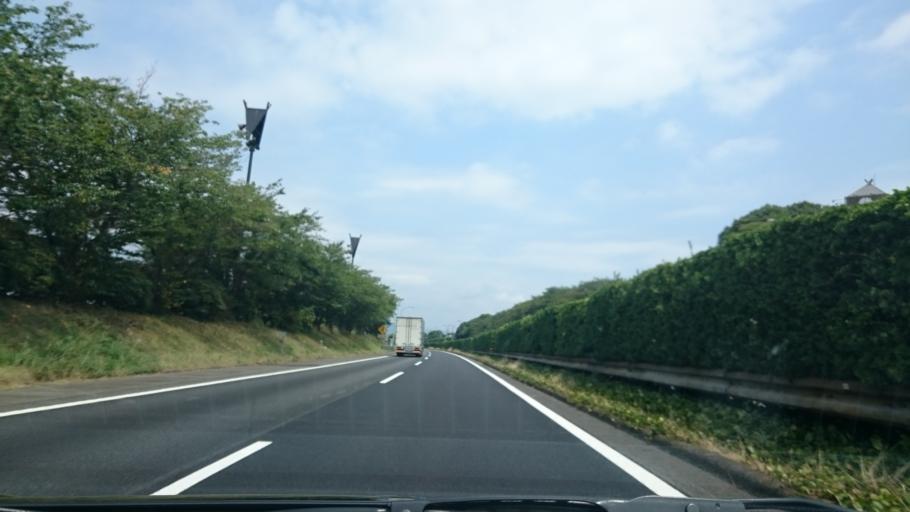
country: JP
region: Shizuoka
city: Shizuoka-shi
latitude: 34.9836
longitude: 138.4341
